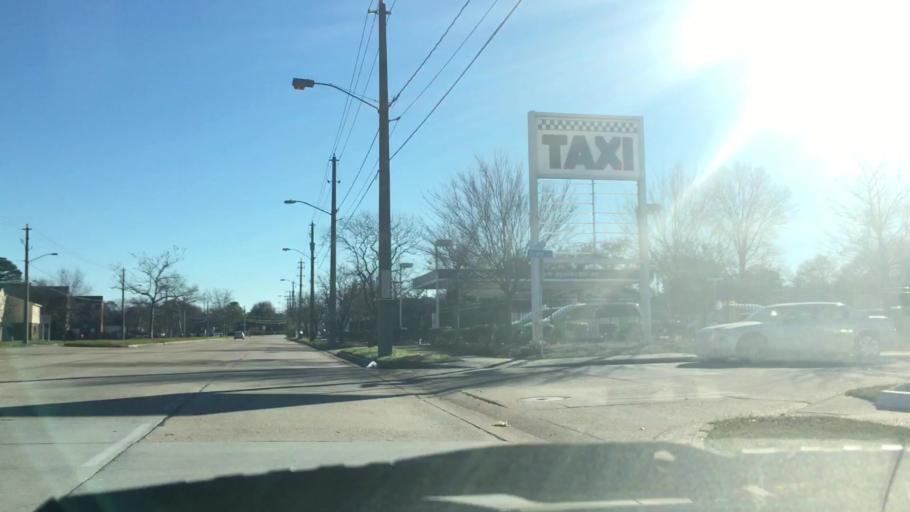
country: US
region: Virginia
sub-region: City of Norfolk
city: Norfolk
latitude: 36.8941
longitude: -76.2383
